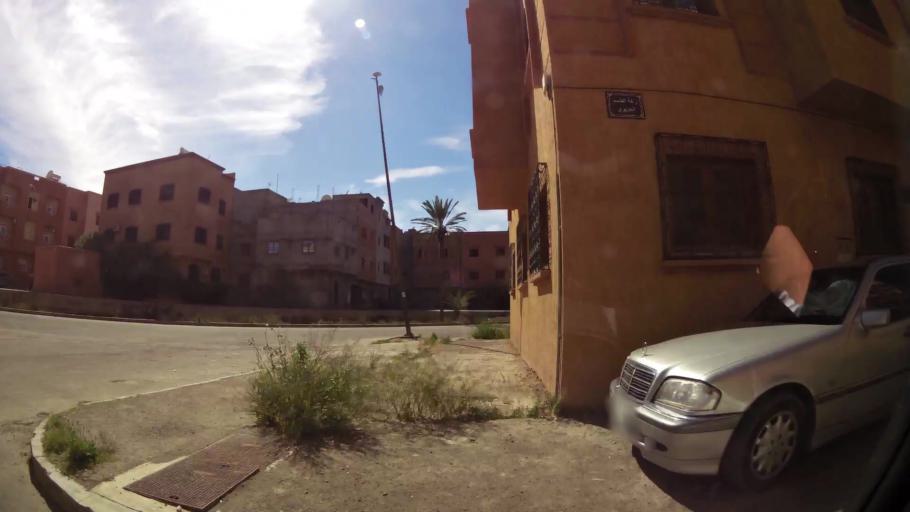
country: MA
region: Marrakech-Tensift-Al Haouz
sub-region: Marrakech
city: Marrakesh
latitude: 31.6694
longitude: -8.0237
